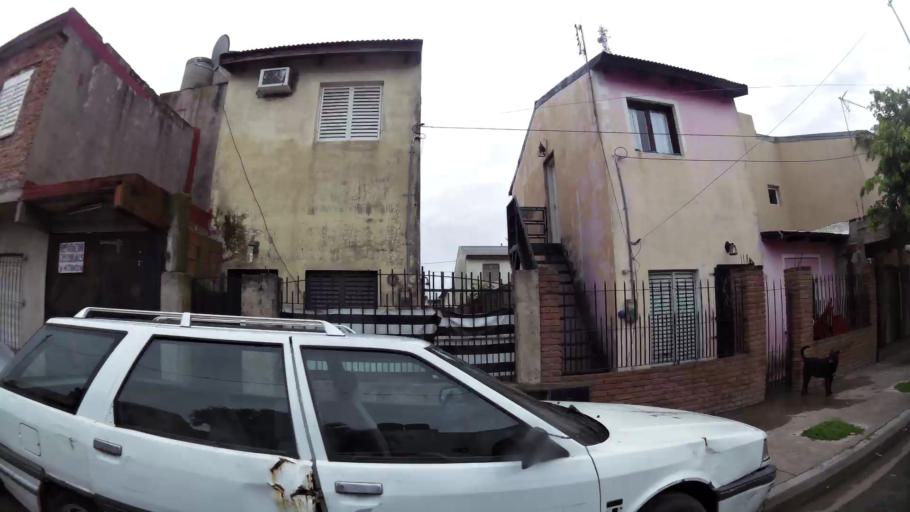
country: AR
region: Buenos Aires
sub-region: Partido de Lanus
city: Lanus
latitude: -34.7331
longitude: -58.3710
